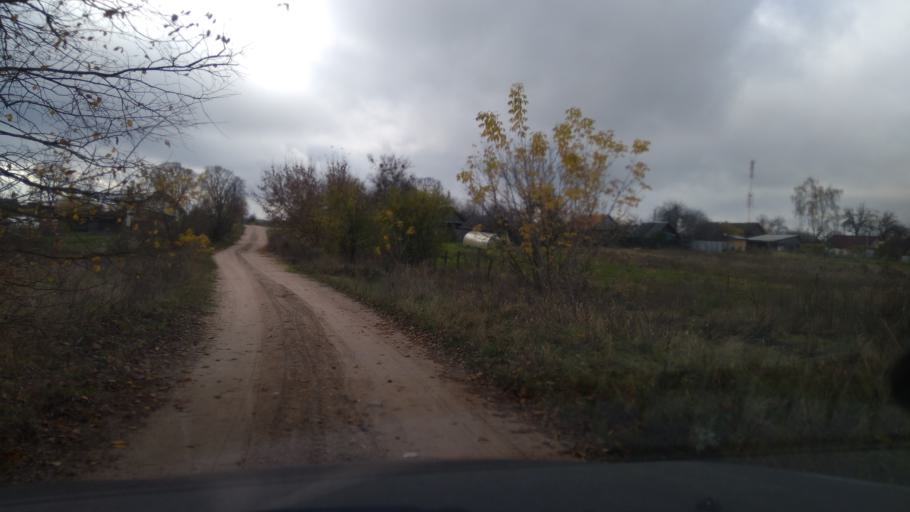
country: BY
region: Minsk
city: Staryya Darohi
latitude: 53.2066
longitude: 28.0495
